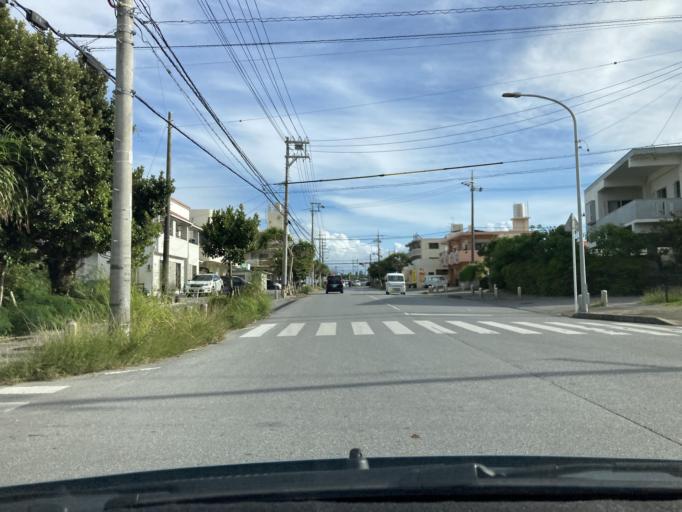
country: JP
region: Okinawa
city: Katsuren-haebaru
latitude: 26.3336
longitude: 127.8384
